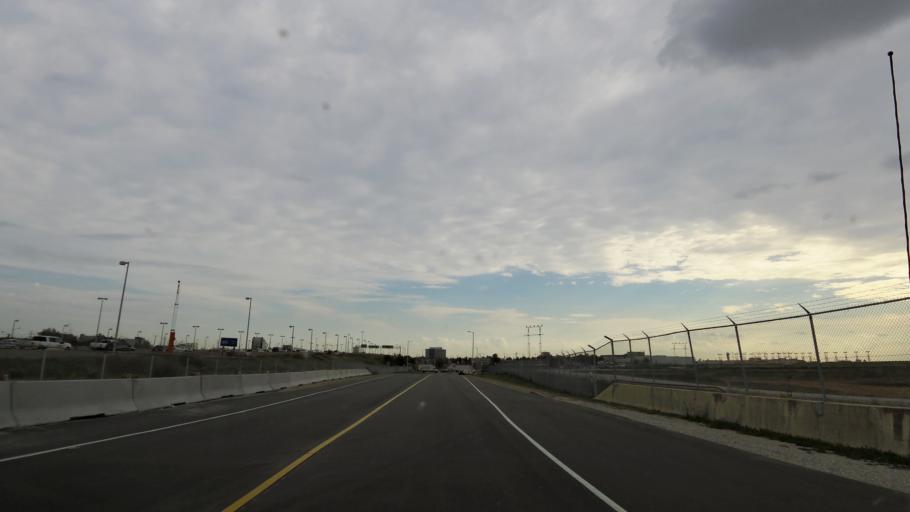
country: CA
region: Ontario
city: Etobicoke
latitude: 43.6786
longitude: -79.5935
